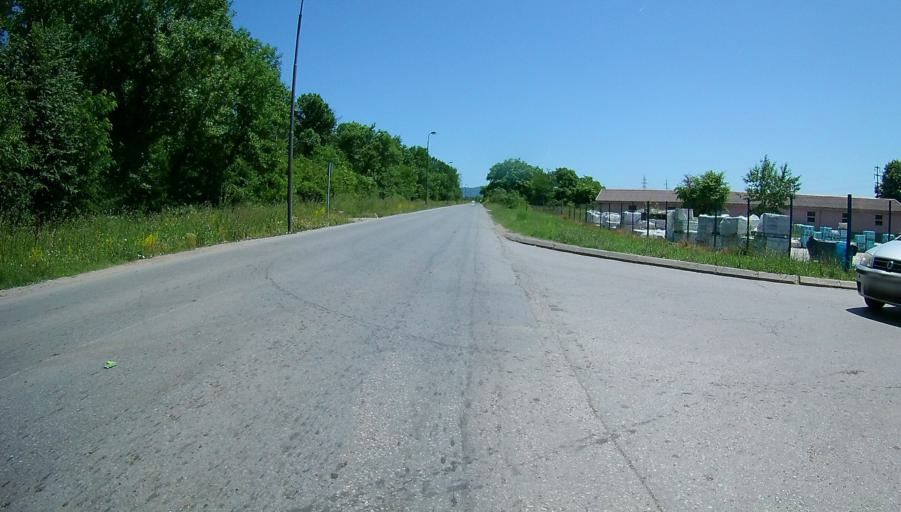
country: RS
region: Central Serbia
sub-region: Nisavski Okrug
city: Nis
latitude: 43.3003
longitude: 21.8749
